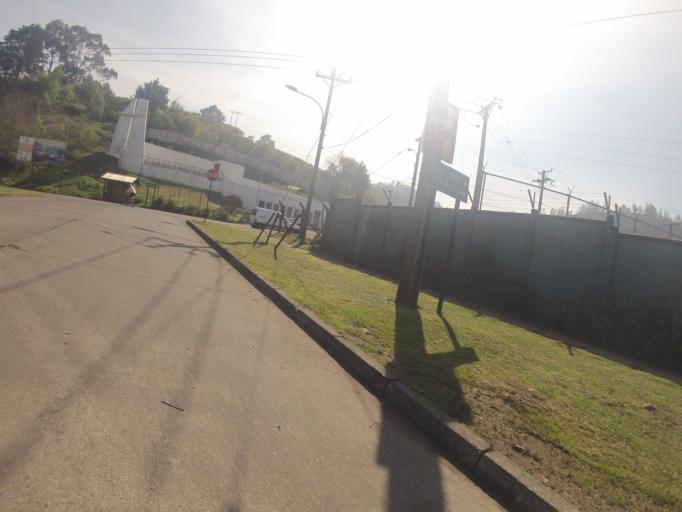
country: CL
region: Araucania
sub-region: Provincia de Cautin
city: Temuco
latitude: -38.7265
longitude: -72.5985
